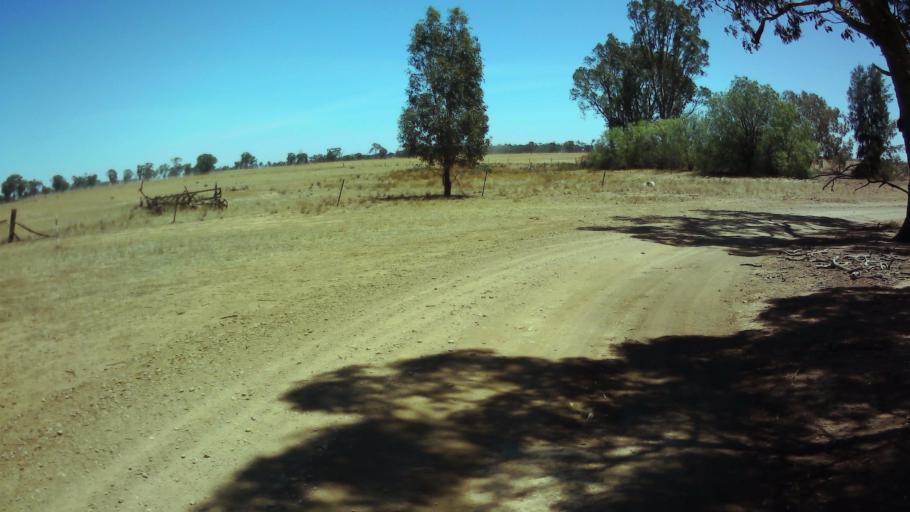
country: AU
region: New South Wales
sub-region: Weddin
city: Grenfell
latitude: -33.9917
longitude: 147.7340
